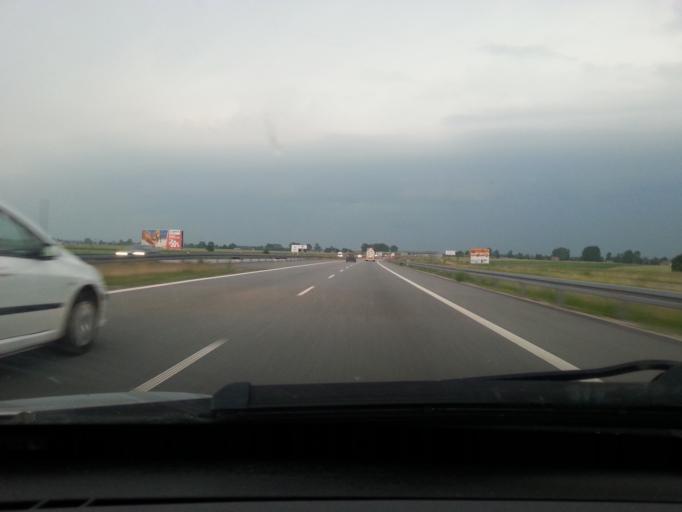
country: PL
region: Lodz Voivodeship
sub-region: powiat Lowicki
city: Lyszkowice
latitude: 52.0080
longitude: 19.9543
